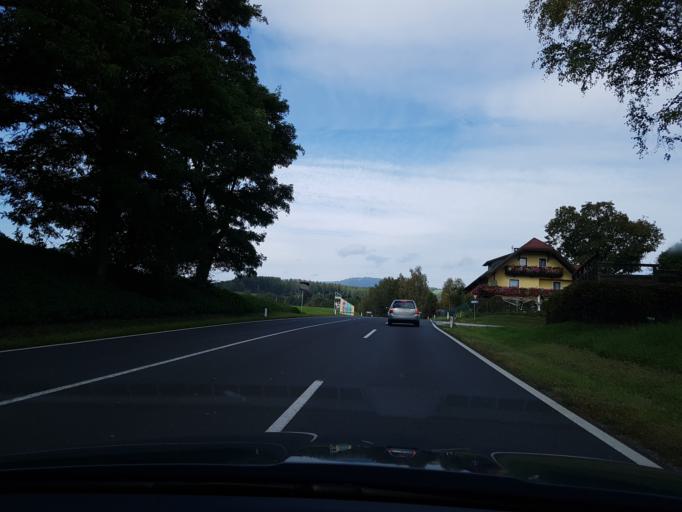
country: AT
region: Carinthia
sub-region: Politischer Bezirk Feldkirchen
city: Feldkirchen in Karnten
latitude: 46.7334
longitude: 14.0737
